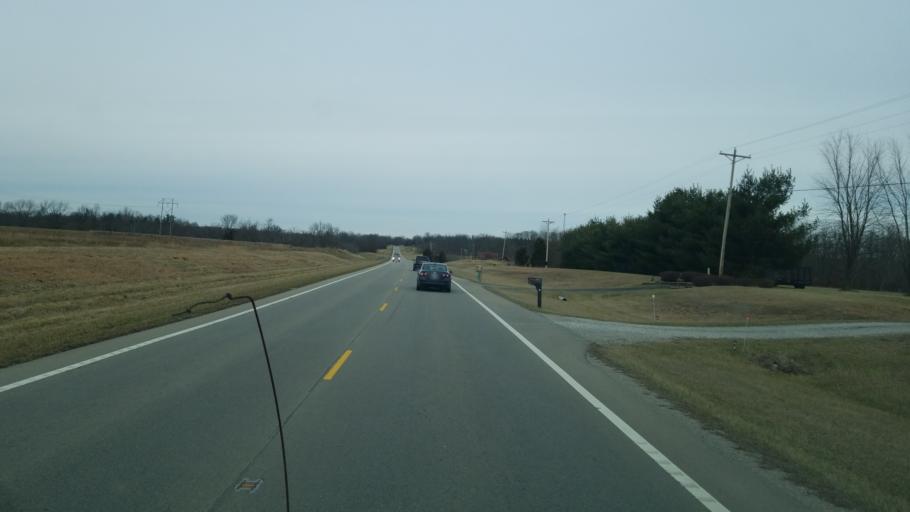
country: US
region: Ohio
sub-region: Highland County
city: Hillsboro
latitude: 39.1019
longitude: -83.6780
